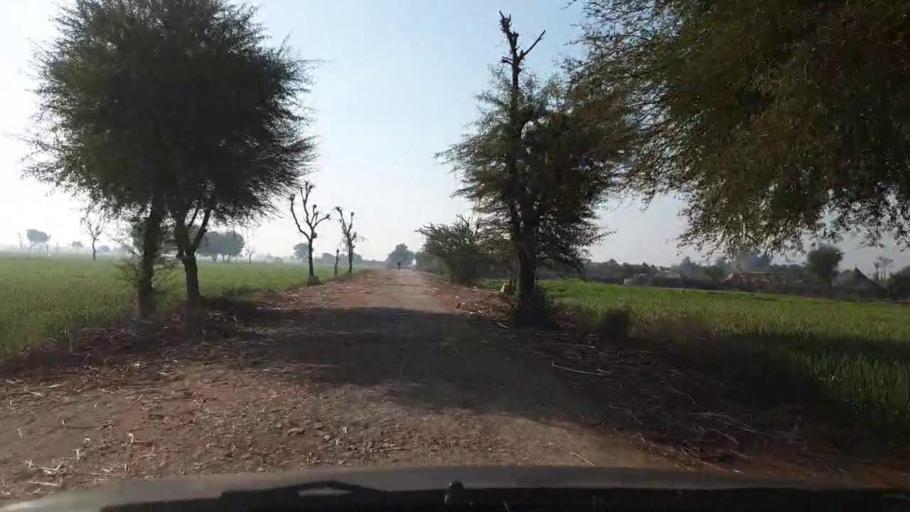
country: PK
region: Sindh
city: Jhol
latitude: 25.9336
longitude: 68.8654
